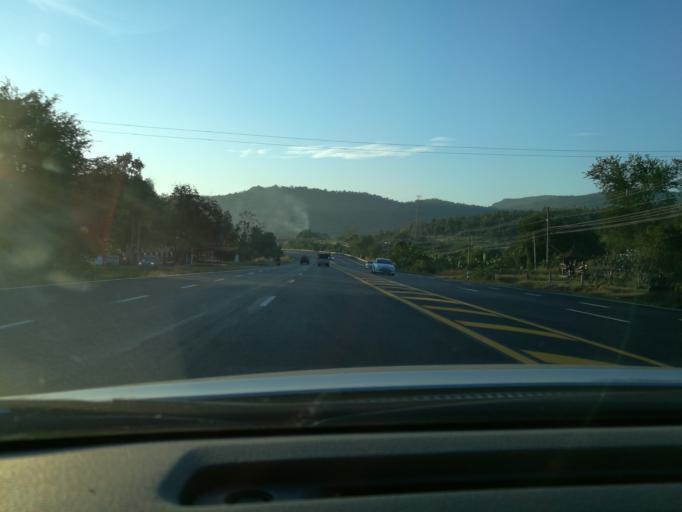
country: TH
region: Phitsanulok
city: Wang Thong
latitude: 16.8659
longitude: 100.4938
